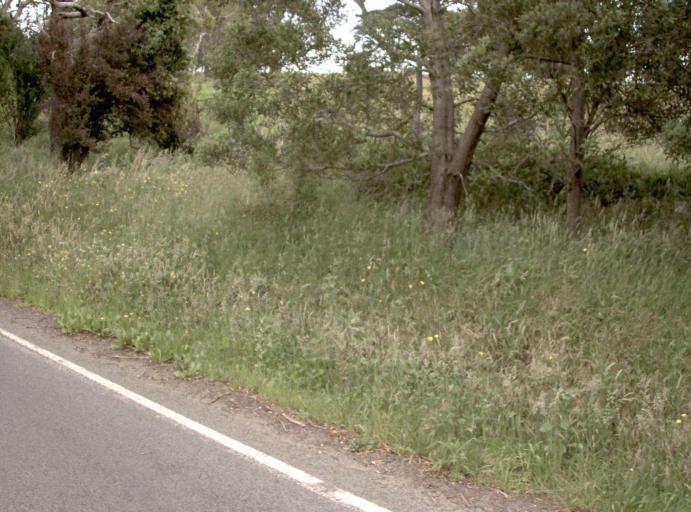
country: AU
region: Victoria
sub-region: Latrobe
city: Moe
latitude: -37.9449
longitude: 146.1196
